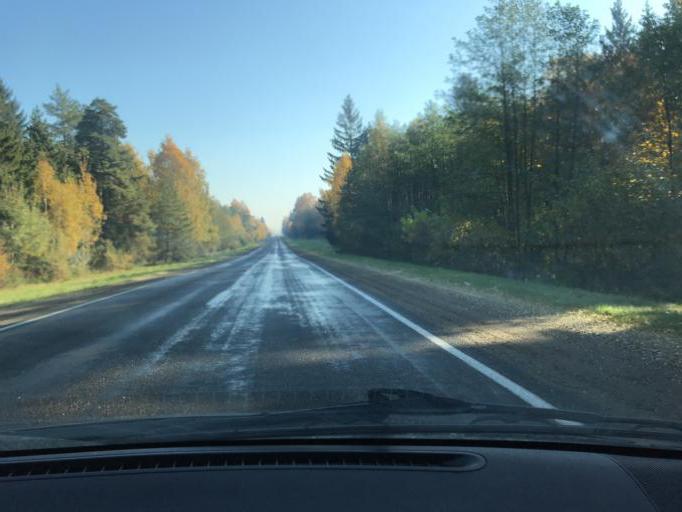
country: BY
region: Brest
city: Lyakhavichy
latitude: 52.9617
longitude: 26.4346
